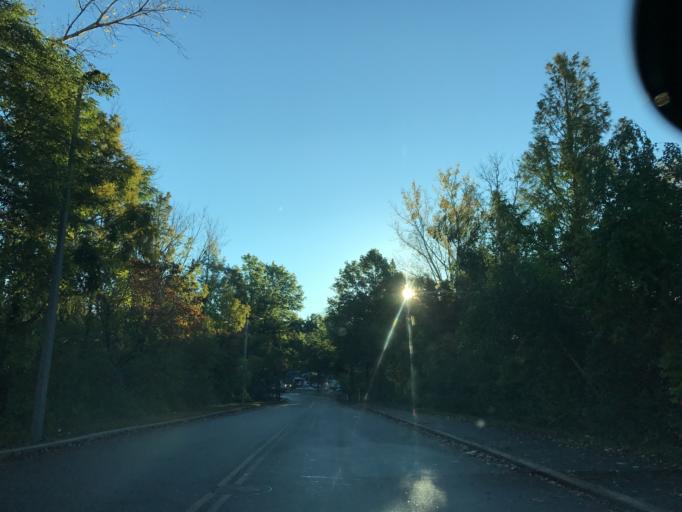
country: US
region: Massachusetts
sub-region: Norfolk County
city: Dedham
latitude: 42.2807
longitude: -71.1731
